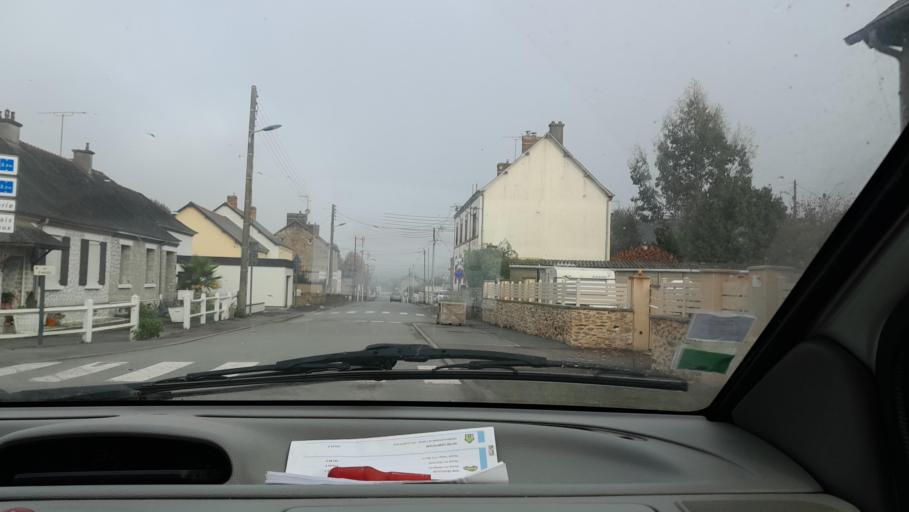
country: FR
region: Pays de la Loire
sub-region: Departement de la Mayenne
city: Saint-Pierre-la-Cour
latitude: 48.1096
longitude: -1.0239
